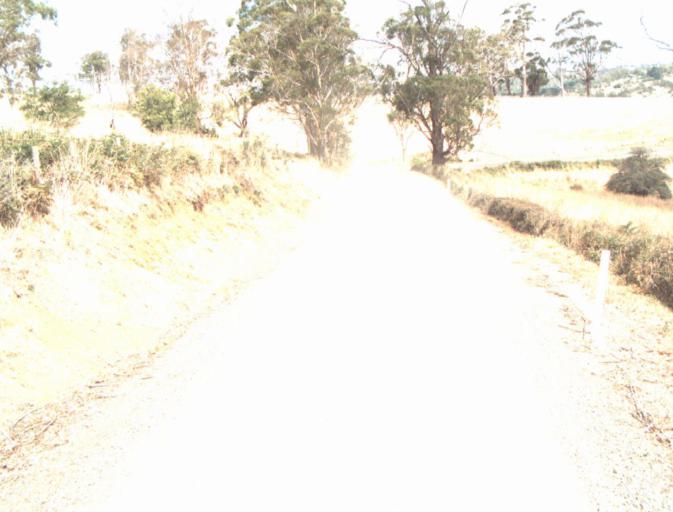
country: AU
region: Tasmania
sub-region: Launceston
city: Mayfield
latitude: -41.3069
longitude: 146.9959
